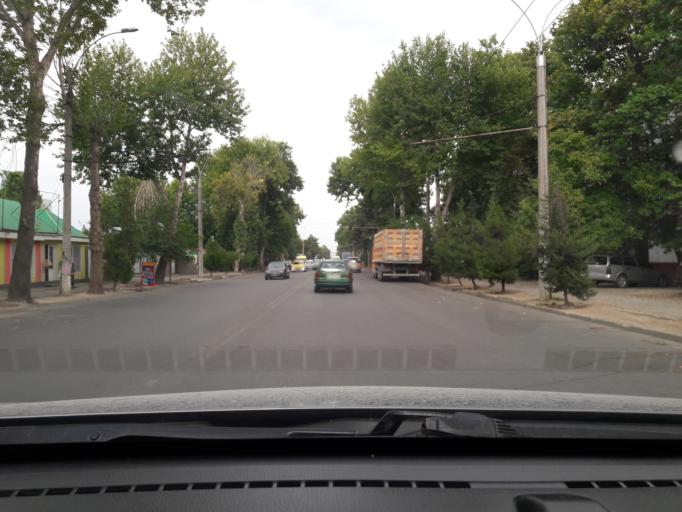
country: TJ
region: Dushanbe
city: Dushanbe
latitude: 38.5461
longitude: 68.7518
